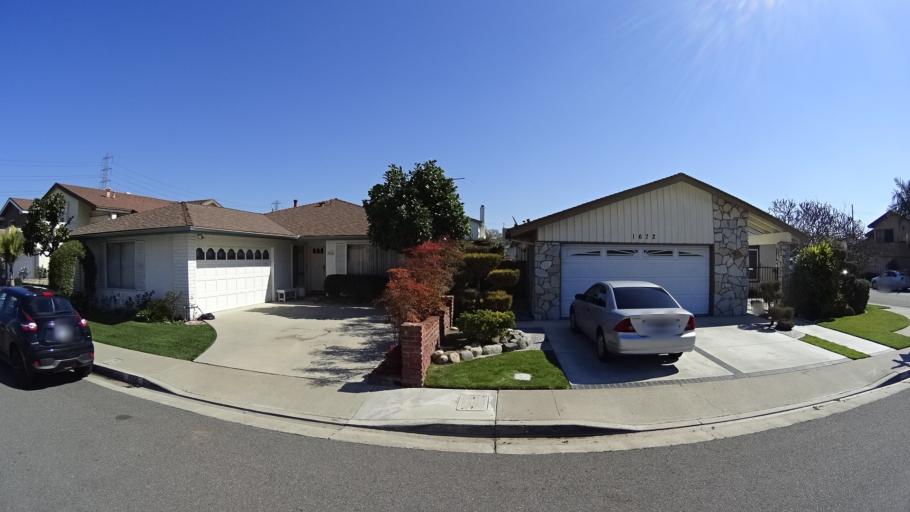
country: US
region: California
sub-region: Orange County
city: Garden Grove
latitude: 33.8056
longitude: -117.9384
